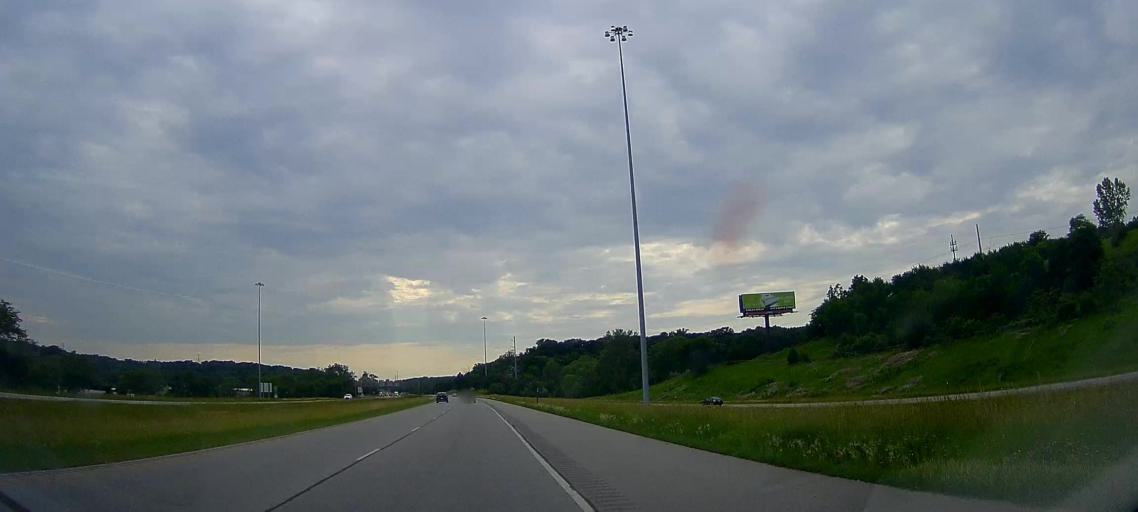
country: US
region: Iowa
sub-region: Pottawattamie County
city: Carter Lake
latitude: 41.3474
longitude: -95.9841
